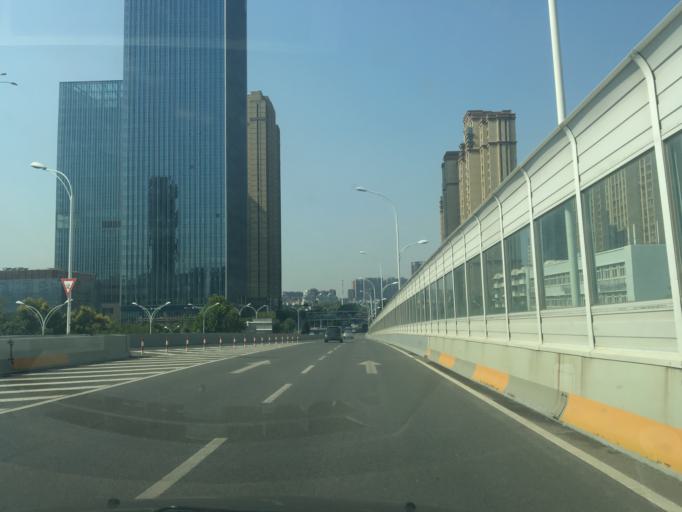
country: CN
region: Hubei
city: Jiang'an
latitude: 30.5727
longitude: 114.3163
